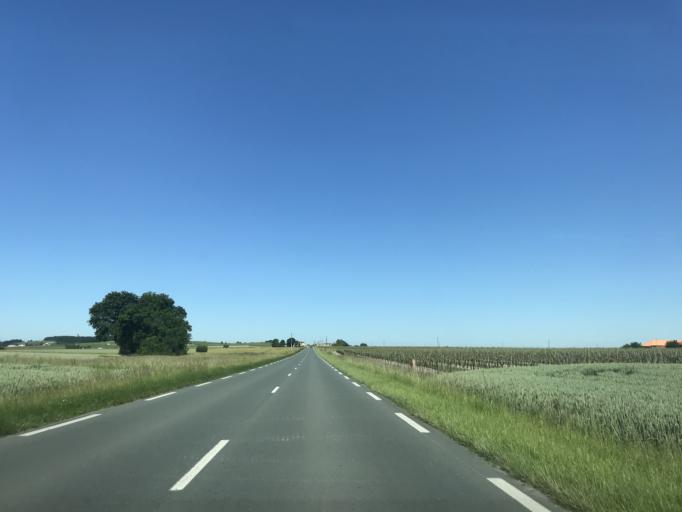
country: FR
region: Poitou-Charentes
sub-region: Departement de la Charente
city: Segonzac
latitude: 45.5330
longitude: -0.3156
